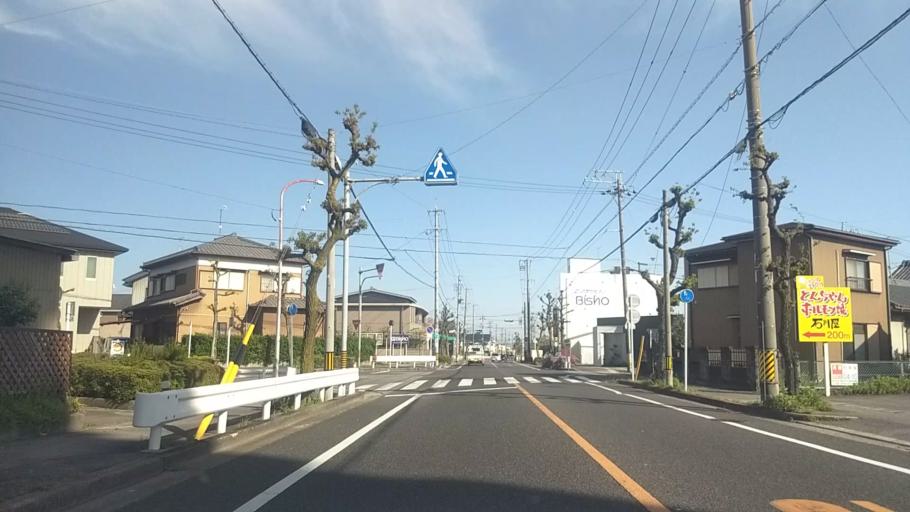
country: JP
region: Aichi
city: Anjo
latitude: 34.9519
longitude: 137.0934
